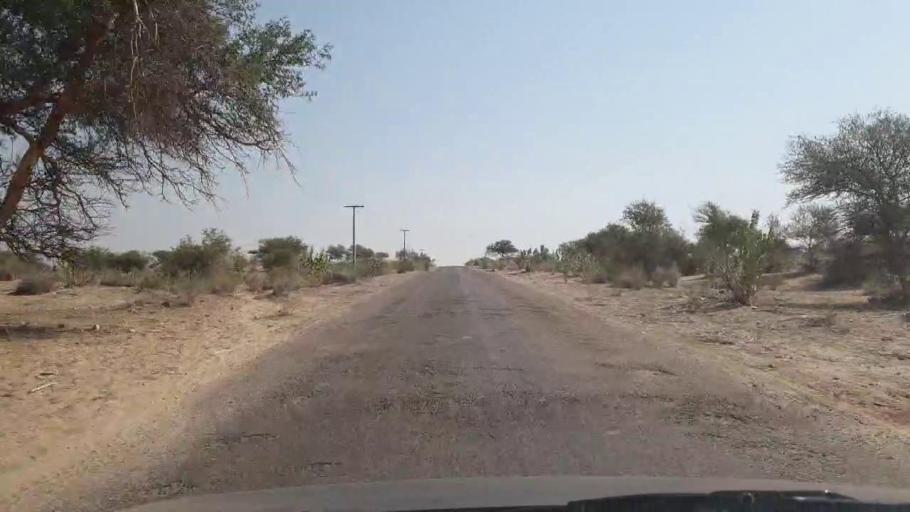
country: PK
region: Sindh
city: Chor
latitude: 25.5944
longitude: 69.9591
